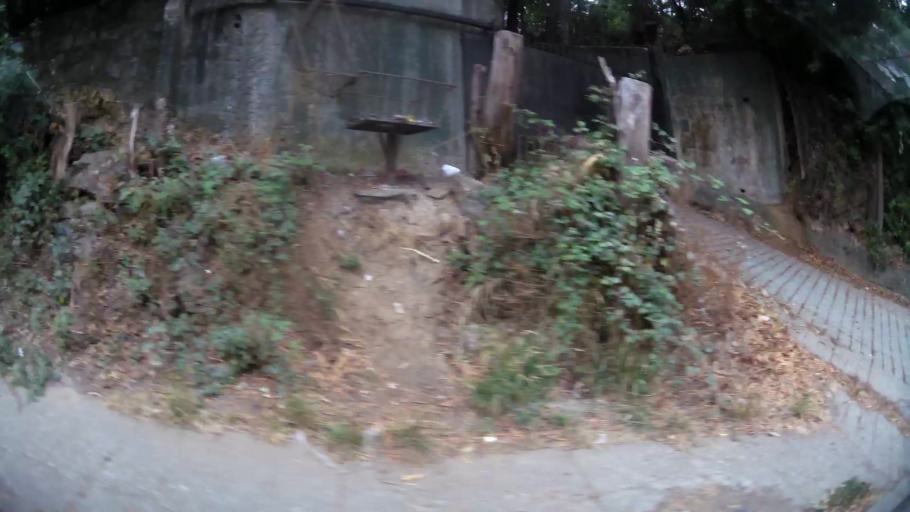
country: CL
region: Biobio
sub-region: Provincia de Concepcion
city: Concepcion
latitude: -36.8341
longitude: -73.0386
